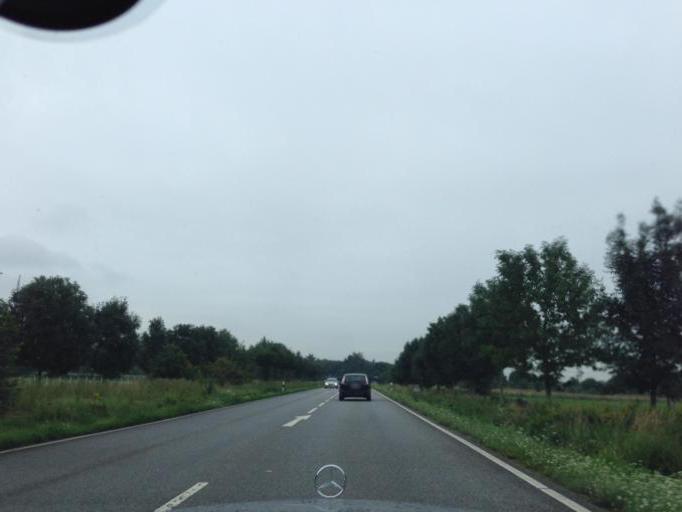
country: DE
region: Schleswig-Holstein
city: Barsbuettel
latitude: 53.5642
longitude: 10.1579
